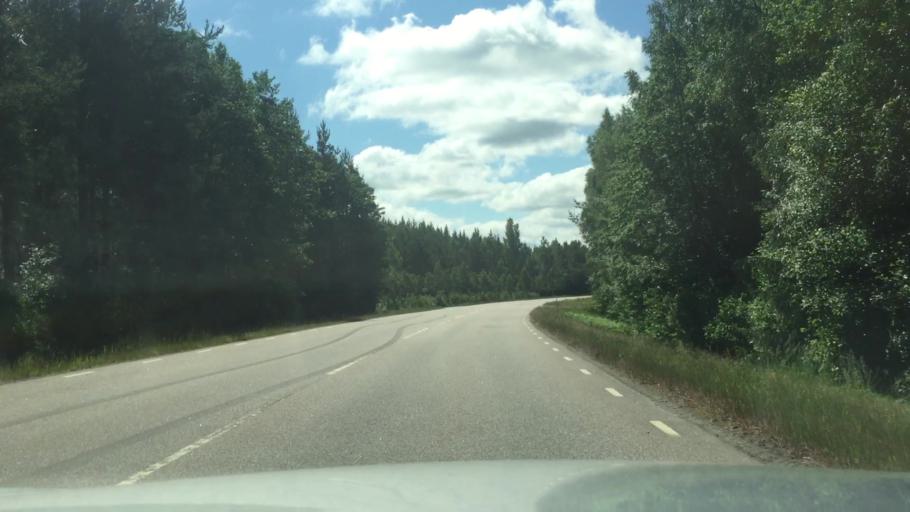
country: SE
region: Vaestra Goetaland
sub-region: Karlsborgs Kommun
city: Molltorp
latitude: 58.6162
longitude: 14.3897
